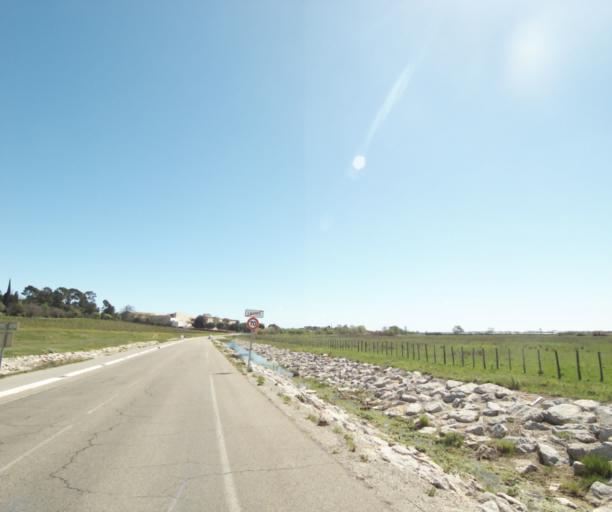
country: FR
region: Languedoc-Roussillon
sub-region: Departement de l'Herault
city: Lattes
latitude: 43.5645
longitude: 3.9183
